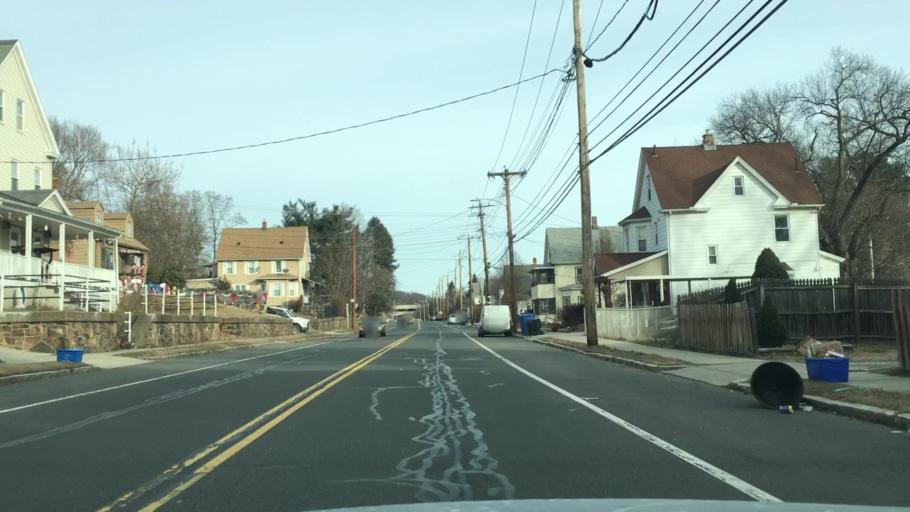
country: US
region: Massachusetts
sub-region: Hampden County
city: North Chicopee
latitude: 42.1733
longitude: -72.6315
